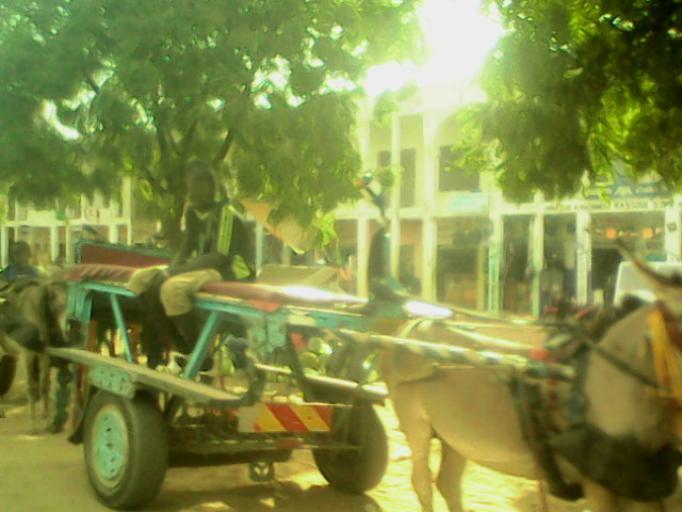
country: SN
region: Diourbel
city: Touba
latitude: 14.8771
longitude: -15.9009
